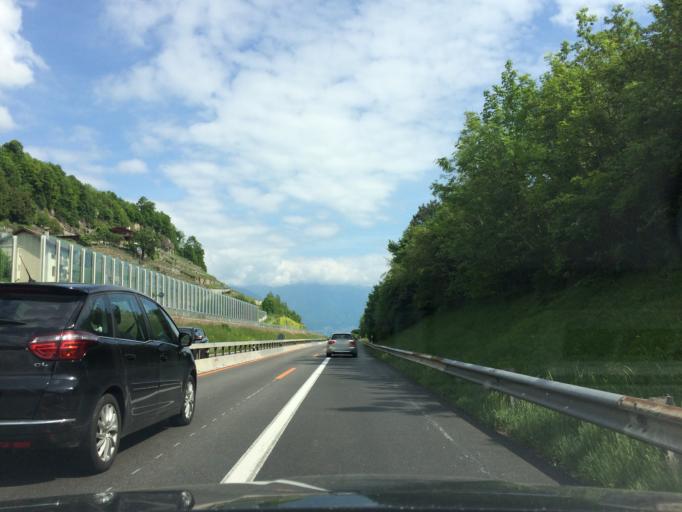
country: CH
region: Vaud
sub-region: Lavaux-Oron District
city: Chexbres
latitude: 46.4801
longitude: 6.7920
